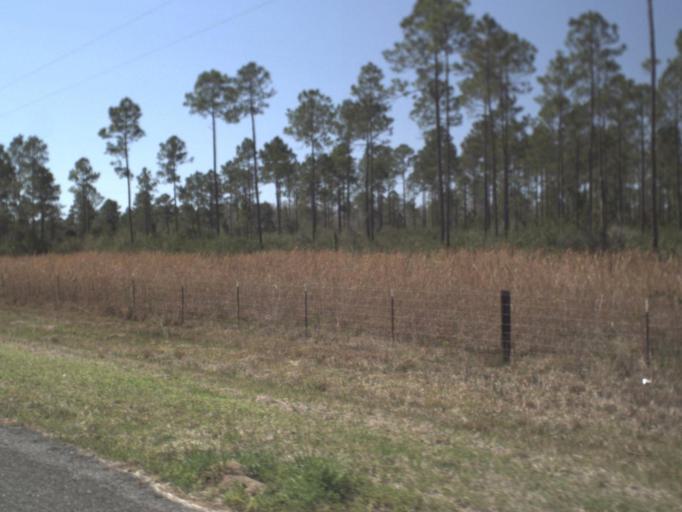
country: US
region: Florida
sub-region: Leon County
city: Woodville
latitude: 30.2420
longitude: -84.0427
